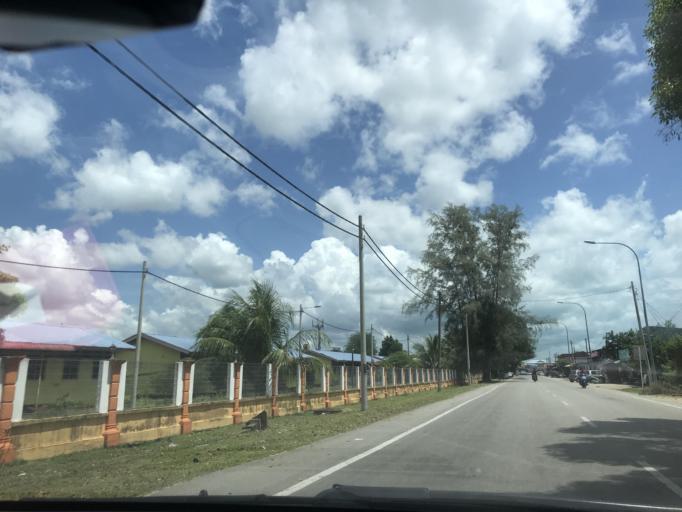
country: TH
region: Narathiwat
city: Tak Bai
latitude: 6.2312
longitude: 102.0942
